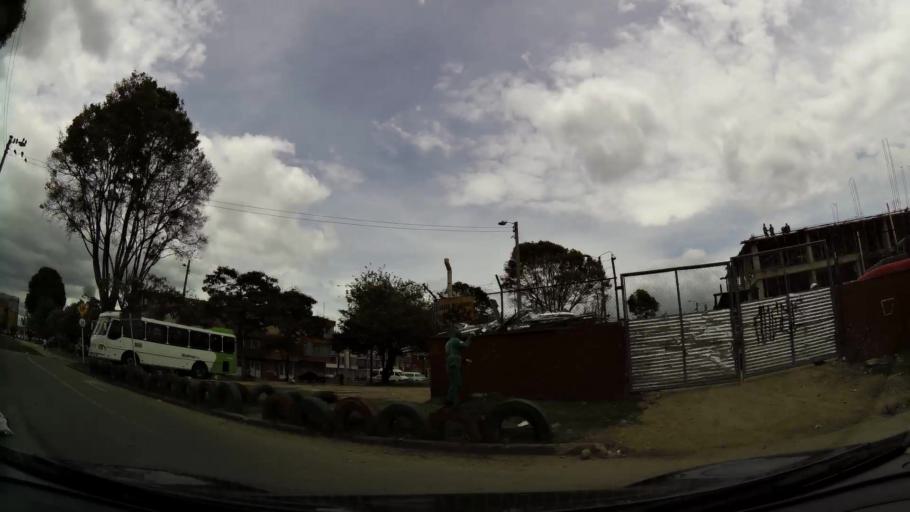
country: CO
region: Cundinamarca
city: Funza
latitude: 4.7114
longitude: -74.1225
